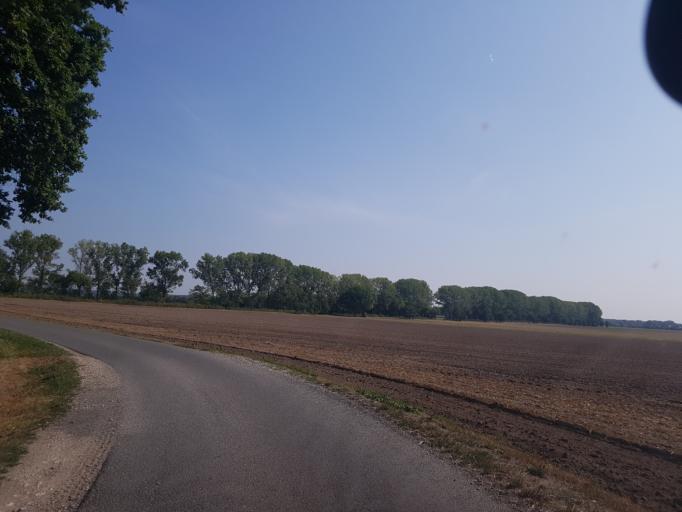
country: DE
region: Brandenburg
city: Sonnewalde
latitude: 51.6856
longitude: 13.6970
